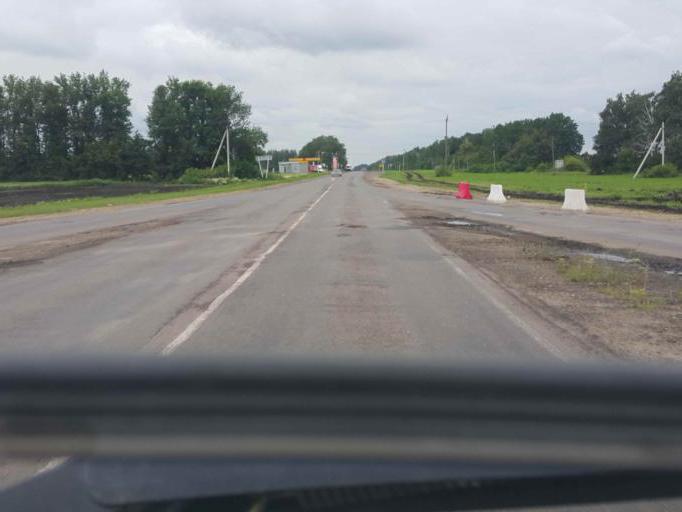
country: RU
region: Tambov
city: Zavoronezhskoye
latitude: 52.9084
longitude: 40.6291
